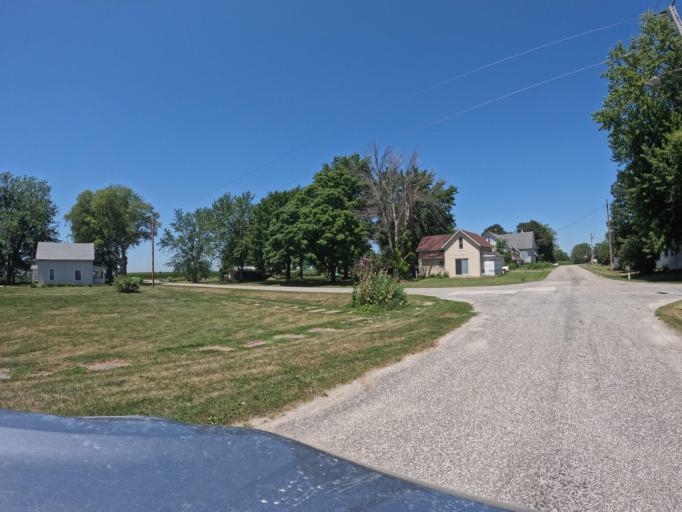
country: US
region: Iowa
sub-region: Keokuk County
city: Sigourney
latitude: 41.4543
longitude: -92.3345
